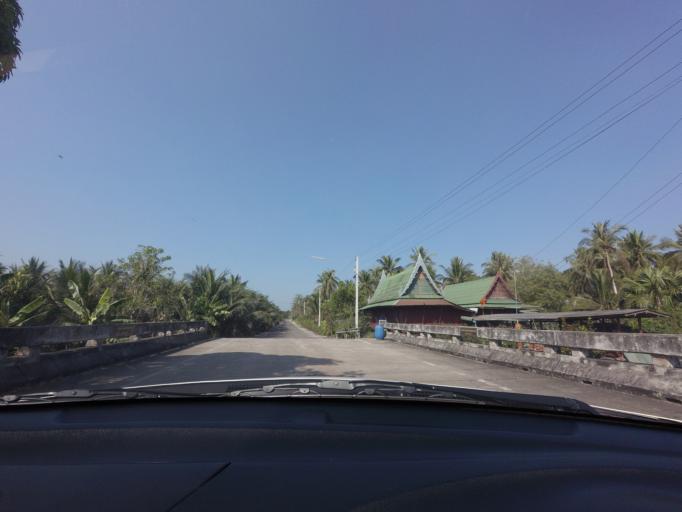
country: TH
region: Ratchaburi
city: Damnoen Saduak
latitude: 13.4831
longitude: 99.9926
